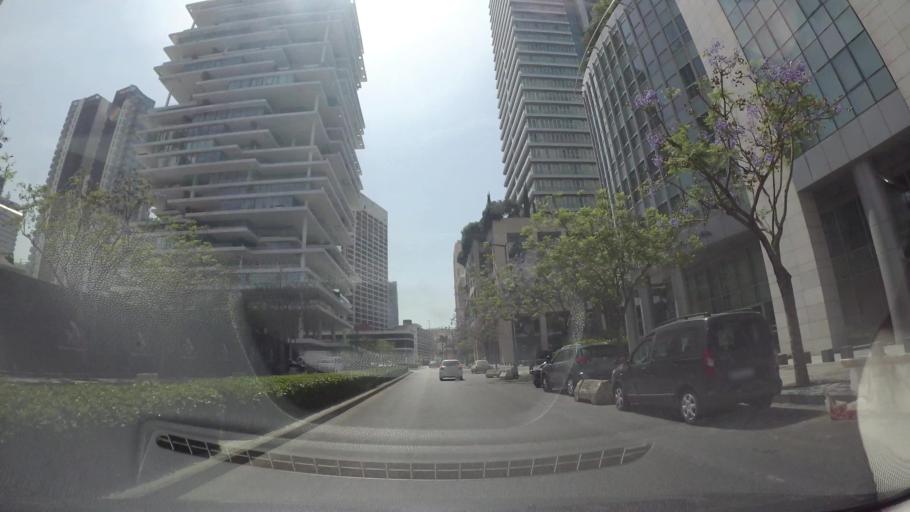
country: LB
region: Beyrouth
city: Beirut
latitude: 33.9002
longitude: 35.4974
